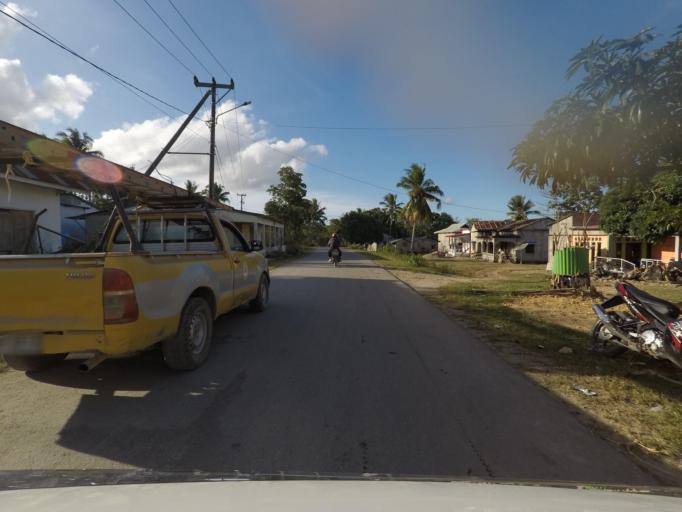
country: TL
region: Lautem
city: Lospalos
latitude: -8.4428
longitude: 127.0059
